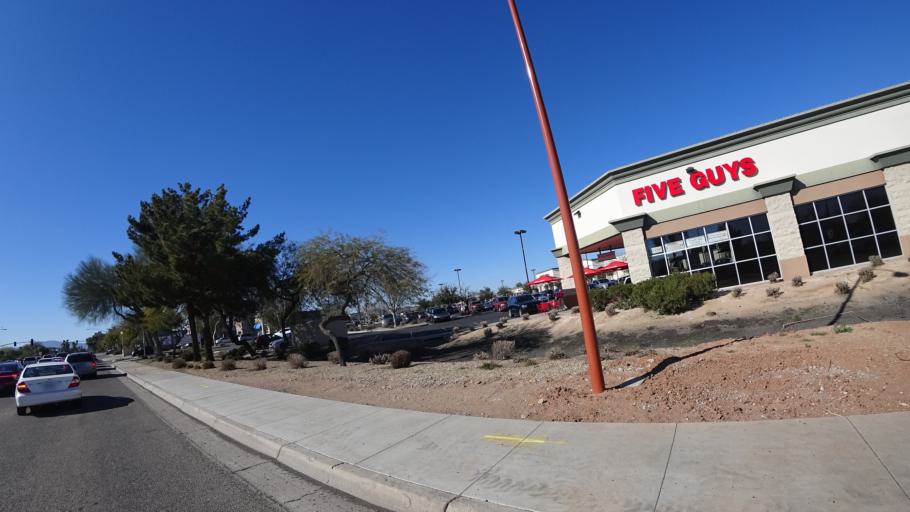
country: US
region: Arizona
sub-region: Maricopa County
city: Surprise
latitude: 33.6388
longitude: -112.3533
